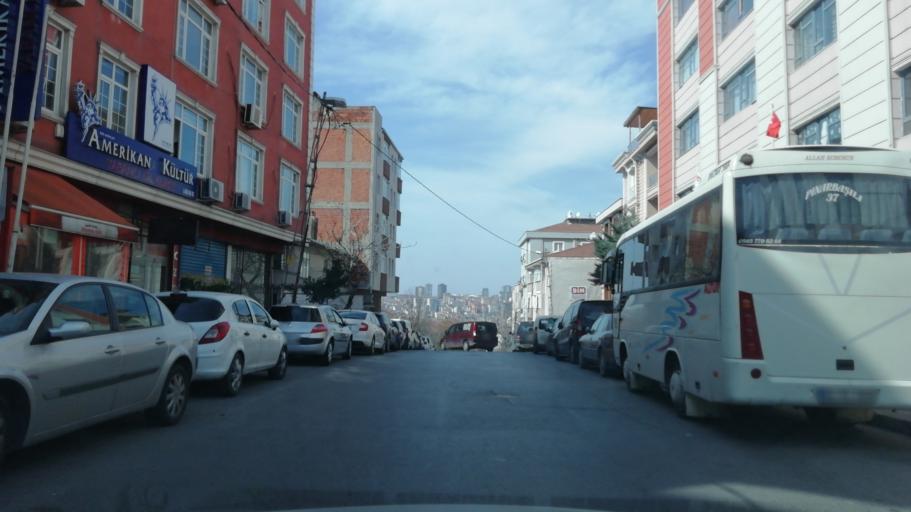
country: TR
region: Istanbul
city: Bagcilar
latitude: 41.0328
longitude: 28.8559
